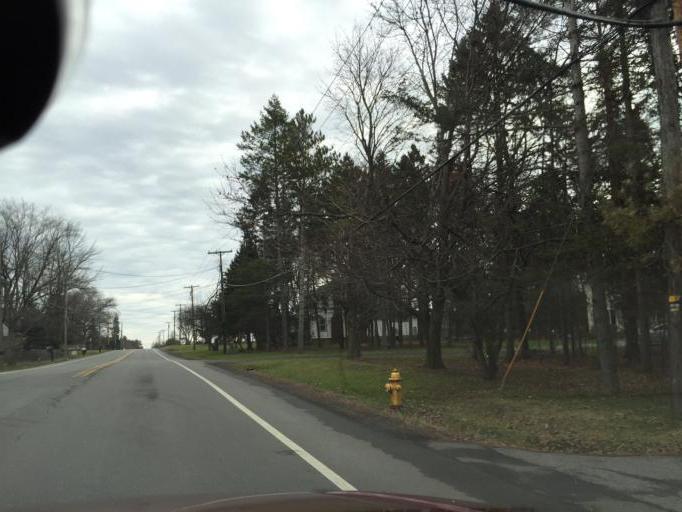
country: US
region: New York
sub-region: Monroe County
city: North Gates
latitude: 43.1063
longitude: -77.7227
